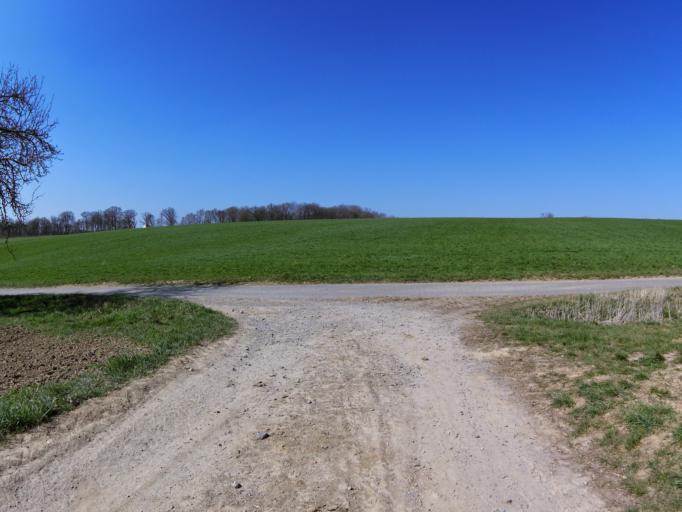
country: DE
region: Bavaria
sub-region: Regierungsbezirk Unterfranken
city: Biebelried
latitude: 49.7675
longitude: 10.0916
